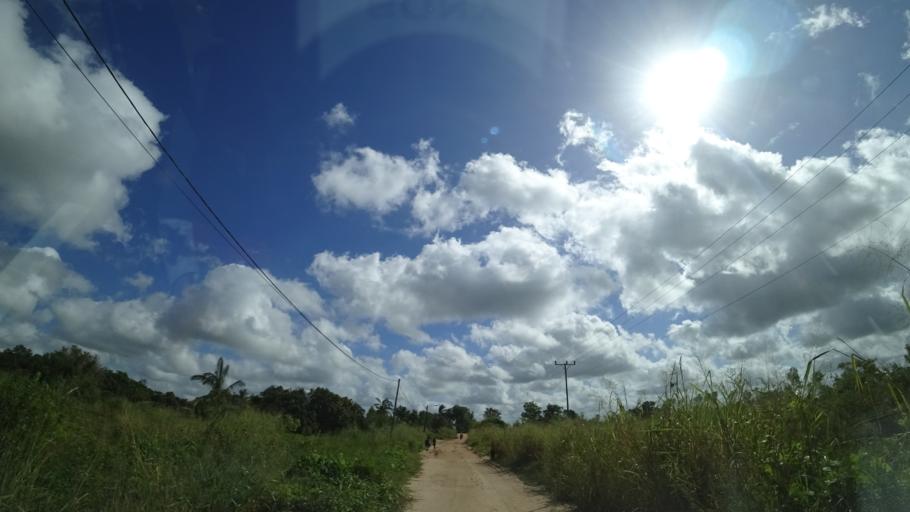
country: MZ
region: Sofala
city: Dondo
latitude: -19.3915
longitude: 34.7085
